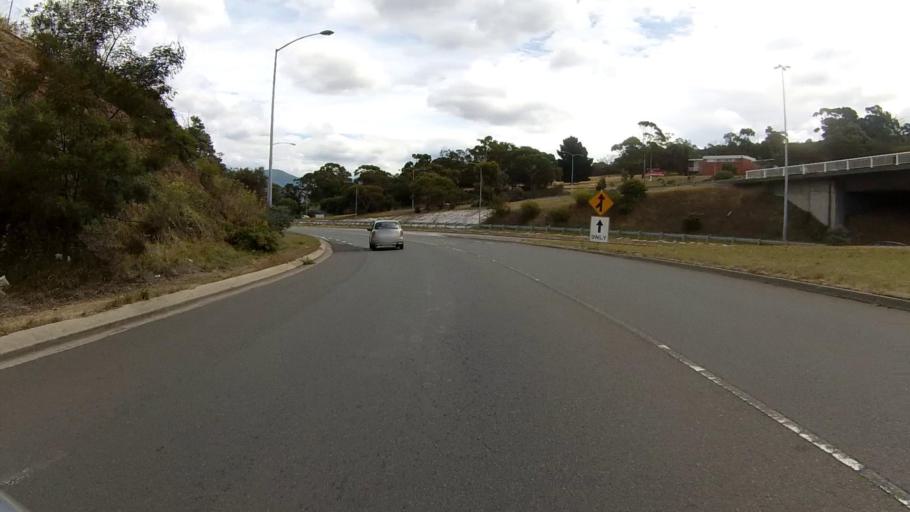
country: AU
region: Tasmania
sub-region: Clarence
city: Lindisfarne
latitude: -42.8627
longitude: 147.3631
